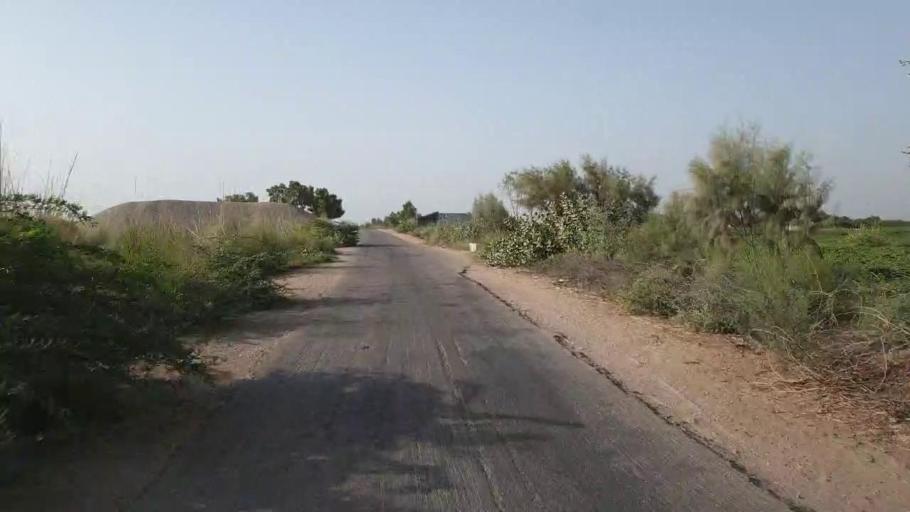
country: PK
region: Sindh
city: Jam Sahib
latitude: 26.4832
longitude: 68.8602
